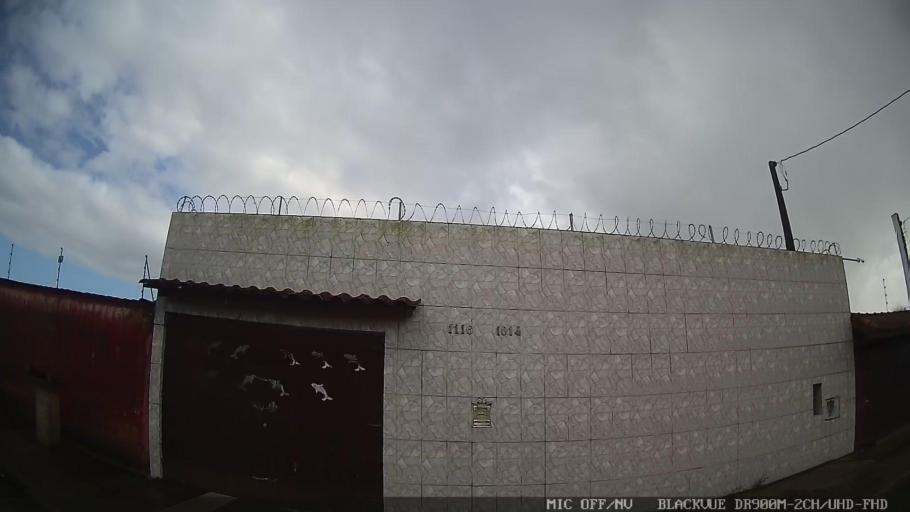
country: BR
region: Sao Paulo
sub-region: Itanhaem
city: Itanhaem
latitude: -24.2036
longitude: -46.8391
